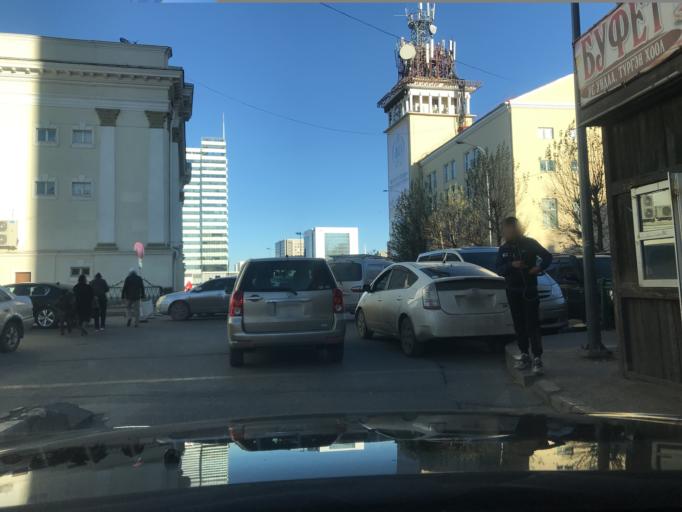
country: MN
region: Ulaanbaatar
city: Ulaanbaatar
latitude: 47.9177
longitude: 106.9151
